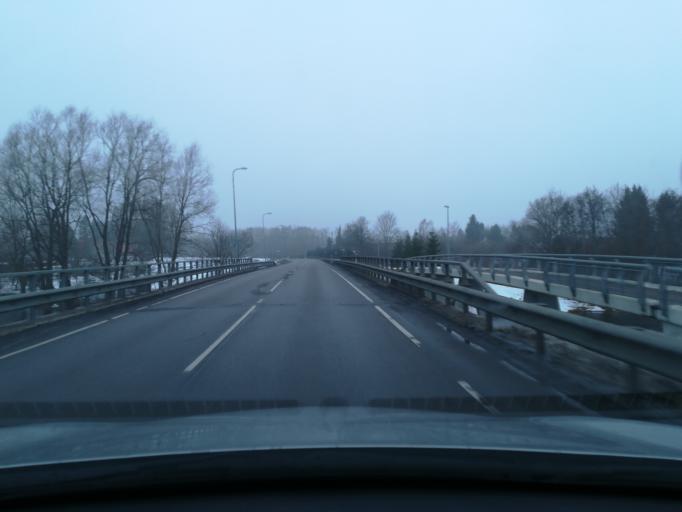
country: EE
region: Harju
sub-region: Rae vald
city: Jueri
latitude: 59.3619
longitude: 24.9481
